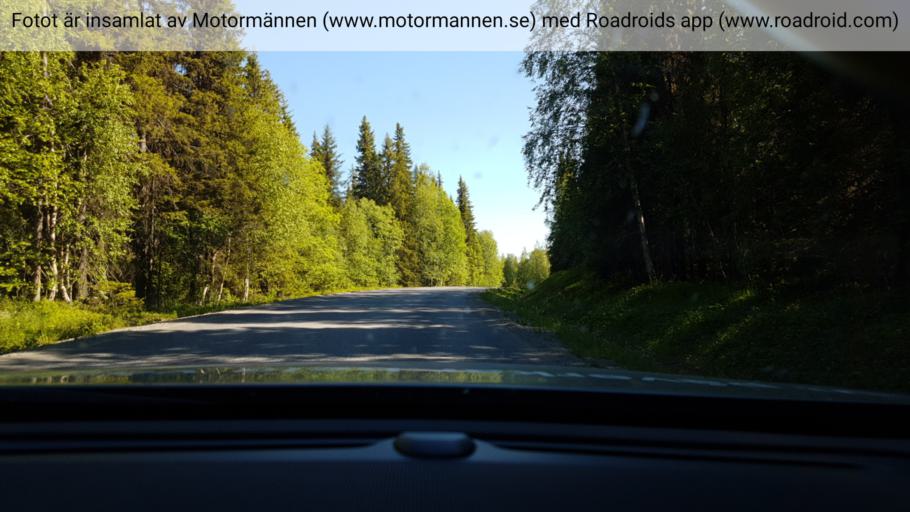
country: SE
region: Vaesterbotten
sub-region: Vilhelmina Kommun
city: Sjoberg
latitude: 64.6560
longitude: 16.3189
